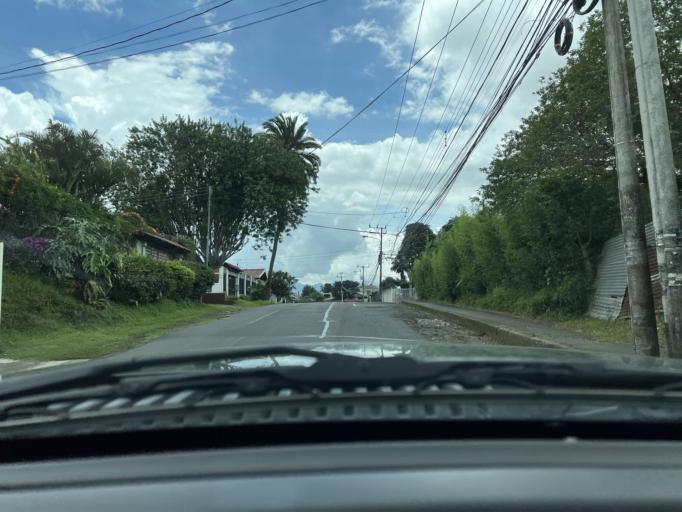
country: CR
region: San Jose
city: Granadilla
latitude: 9.9419
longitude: -84.0240
